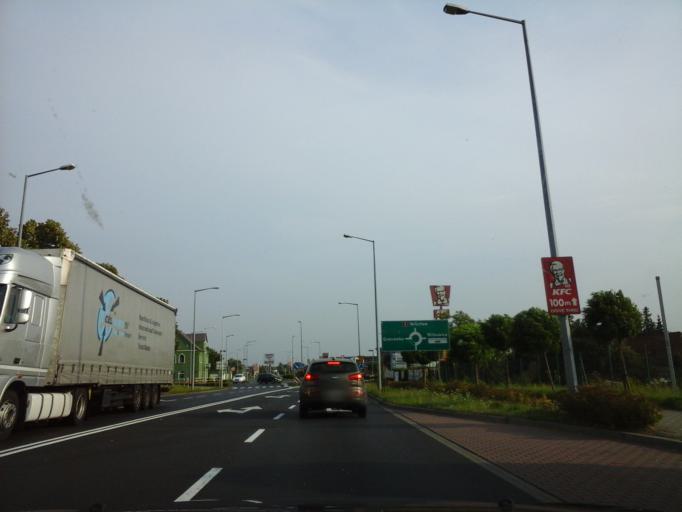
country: PL
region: Greater Poland Voivodeship
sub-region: Leszno
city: Leszno
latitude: 51.8642
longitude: 16.5733
